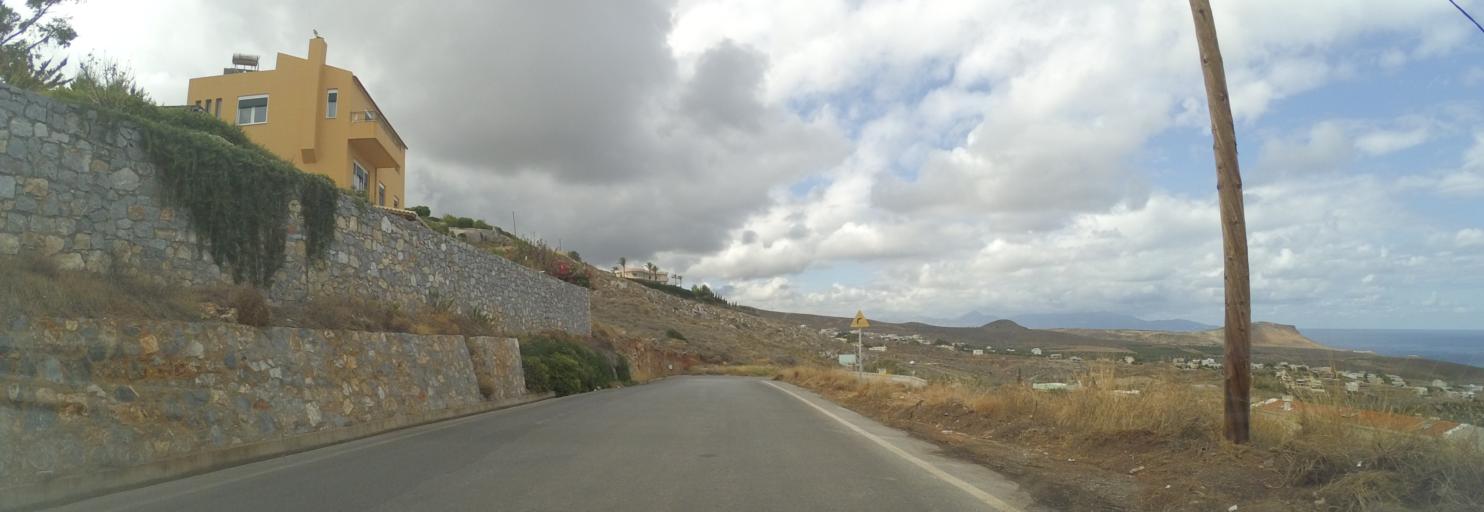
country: GR
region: Crete
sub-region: Nomos Irakleiou
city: Kokkini Hani
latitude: 35.3160
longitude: 25.2532
